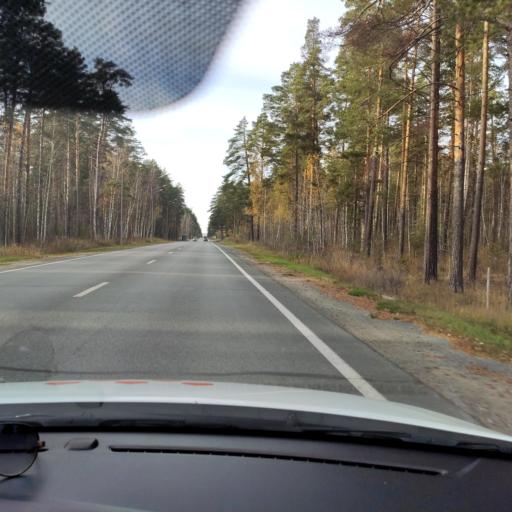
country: RU
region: Tatarstan
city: Stolbishchi
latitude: 55.6359
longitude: 49.0691
